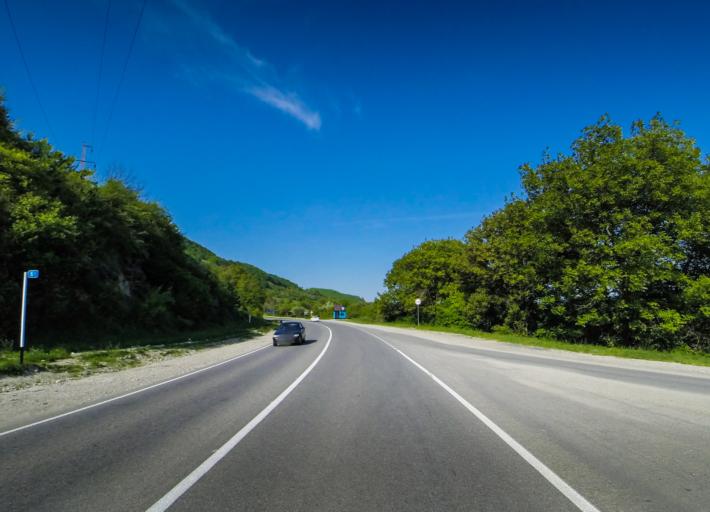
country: RU
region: Kabardino-Balkariya
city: Kashkhatau
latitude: 43.3310
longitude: 43.6460
